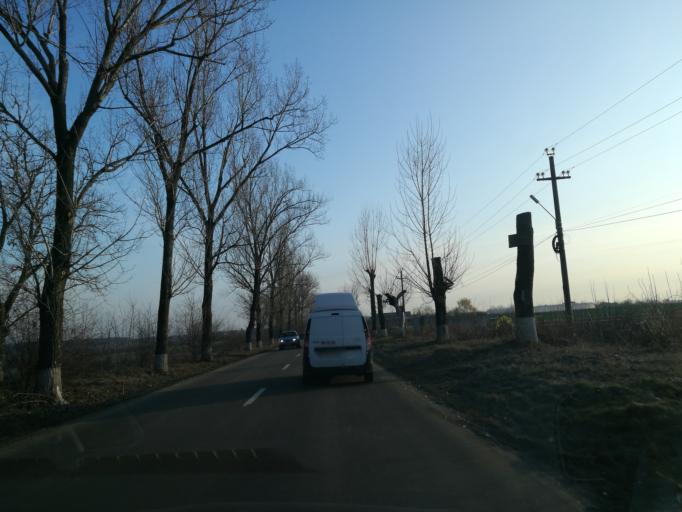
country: RO
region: Ilfov
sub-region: Comuna Moara Vlasiei
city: Caciulati
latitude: 44.6265
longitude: 26.1512
